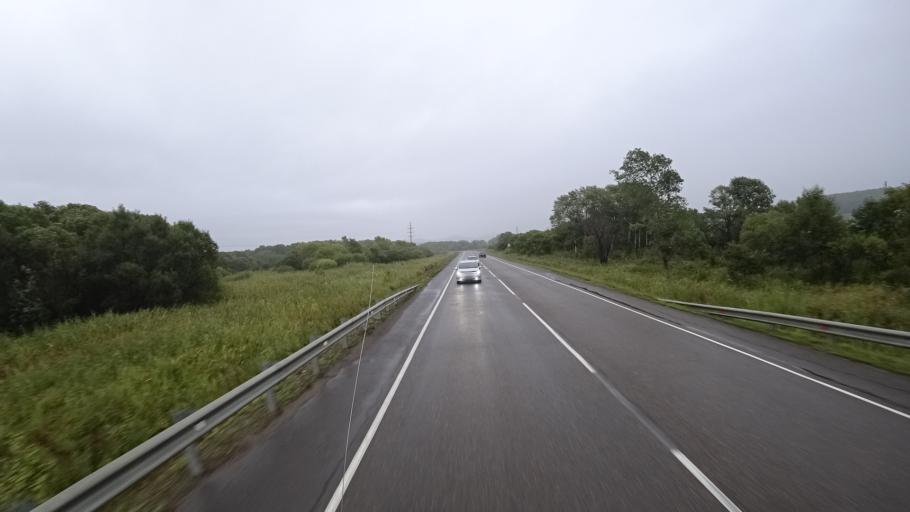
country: RU
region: Primorskiy
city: Monastyrishche
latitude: 44.2762
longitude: 132.4831
